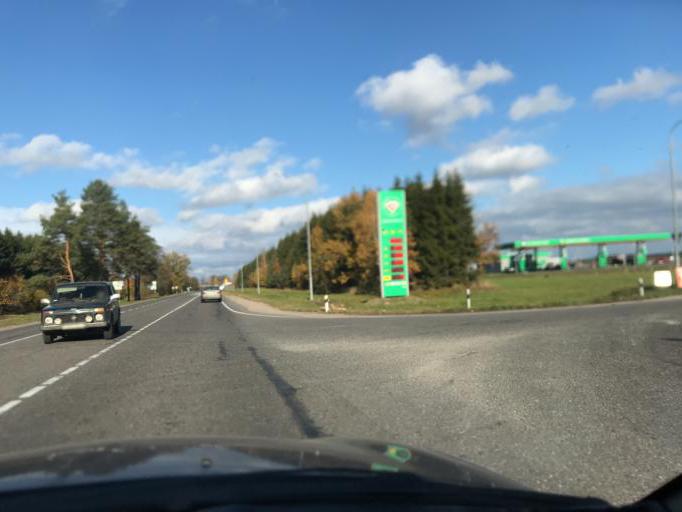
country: LT
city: Salcininkai
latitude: 54.2331
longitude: 25.3575
